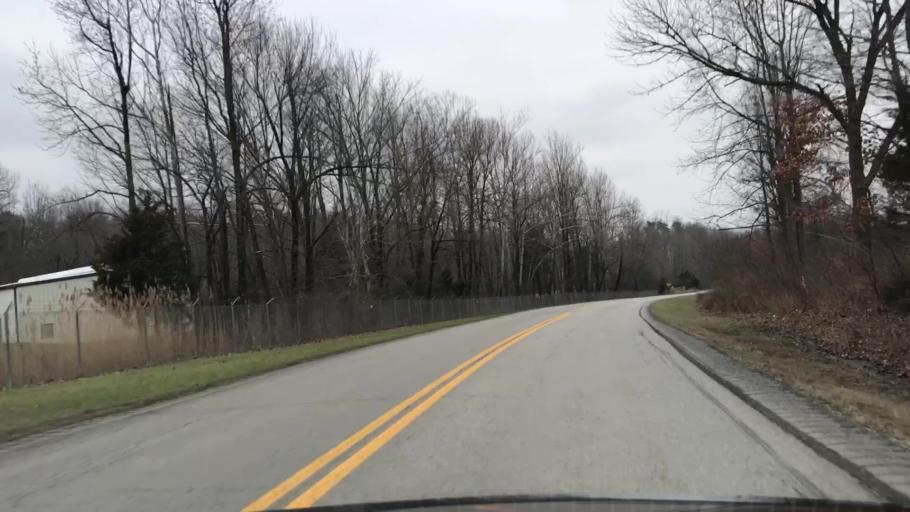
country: US
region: Kentucky
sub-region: Muhlenberg County
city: Morehead
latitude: 37.2610
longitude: -87.2093
